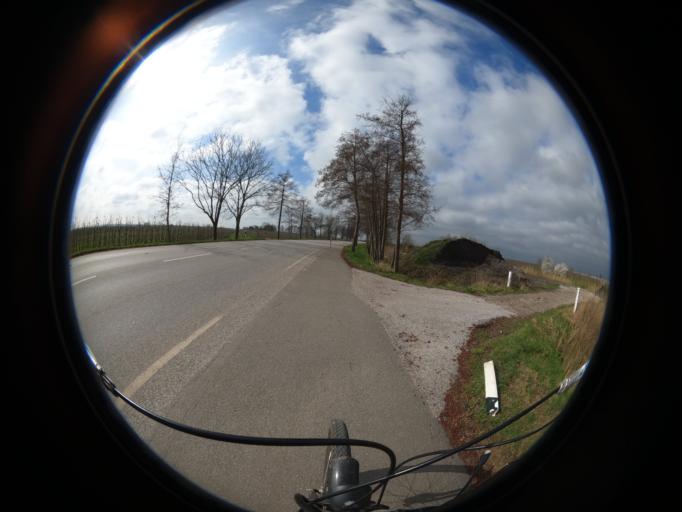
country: DE
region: Lower Saxony
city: Neu Wulmstorf
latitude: 53.5093
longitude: 9.7893
